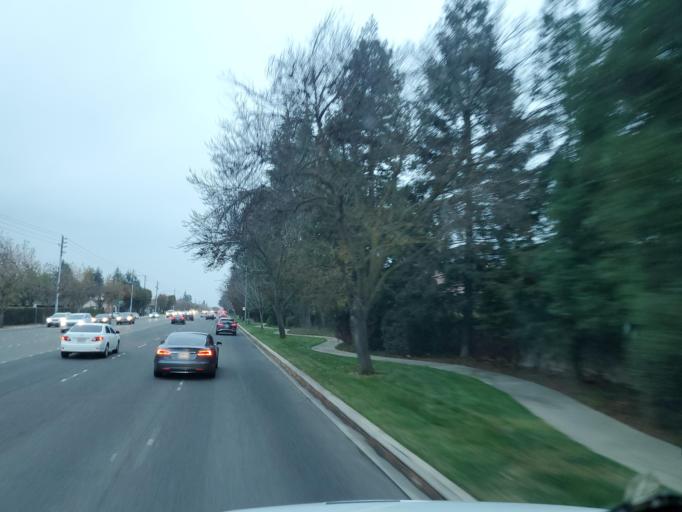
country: US
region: California
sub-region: Stanislaus County
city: Salida
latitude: 37.7004
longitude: -121.0529
